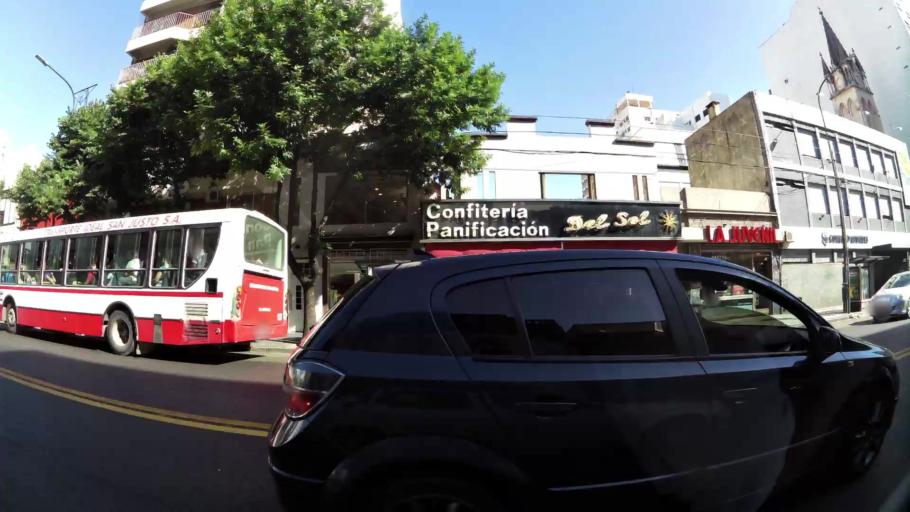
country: AR
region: Buenos Aires F.D.
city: Villa Santa Rita
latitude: -34.6259
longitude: -58.4548
